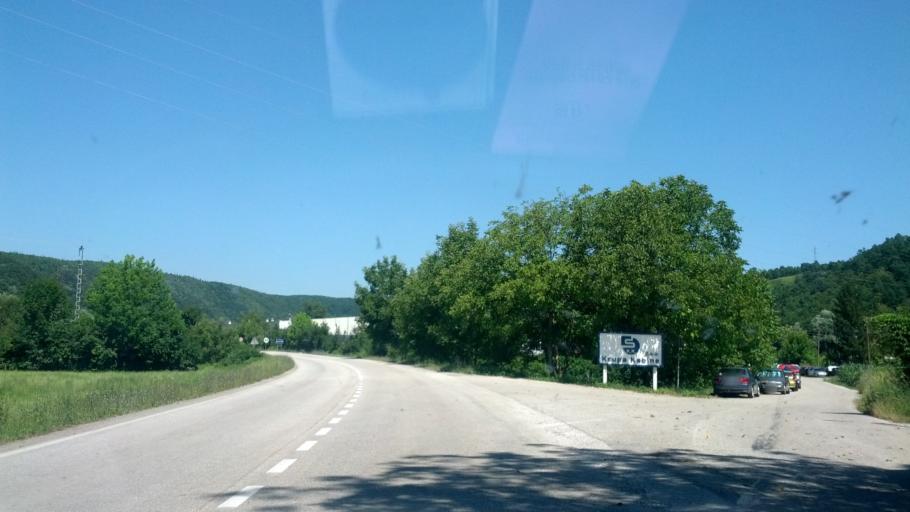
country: BA
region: Federation of Bosnia and Herzegovina
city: Bosanska Krupa
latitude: 44.9058
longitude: 16.1630
